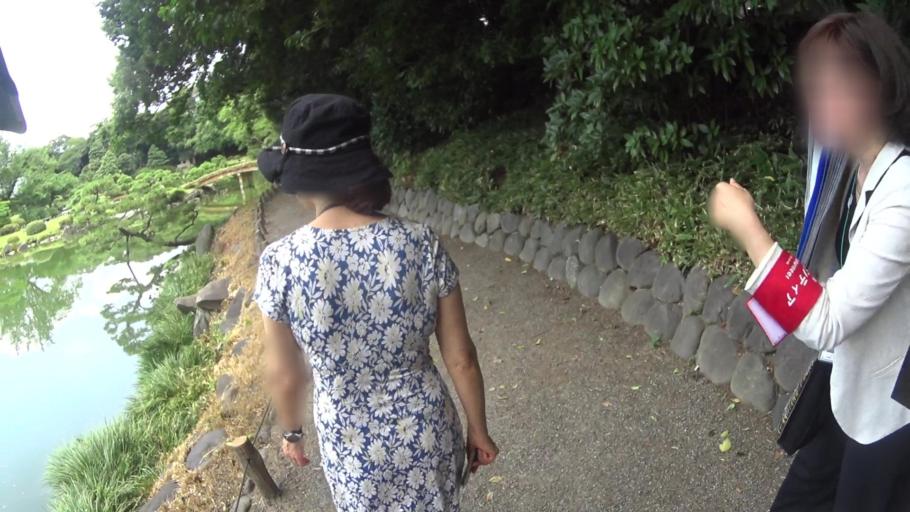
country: JP
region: Tokyo
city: Urayasu
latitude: 35.6797
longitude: 139.7987
